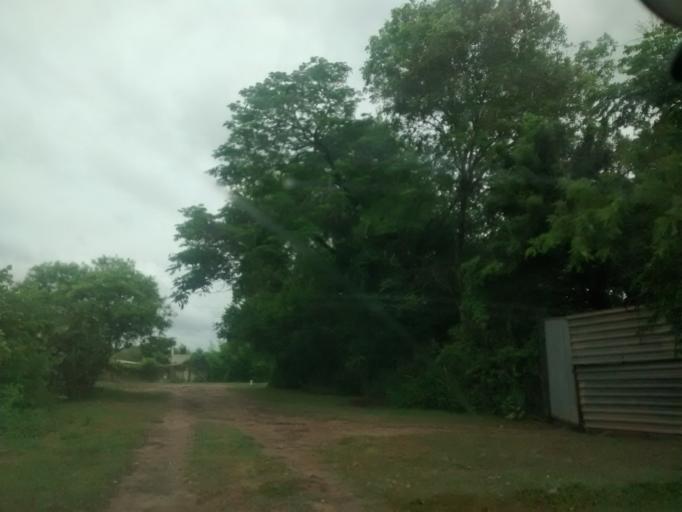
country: AR
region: Chaco
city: Resistencia
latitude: -27.4356
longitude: -58.9726
